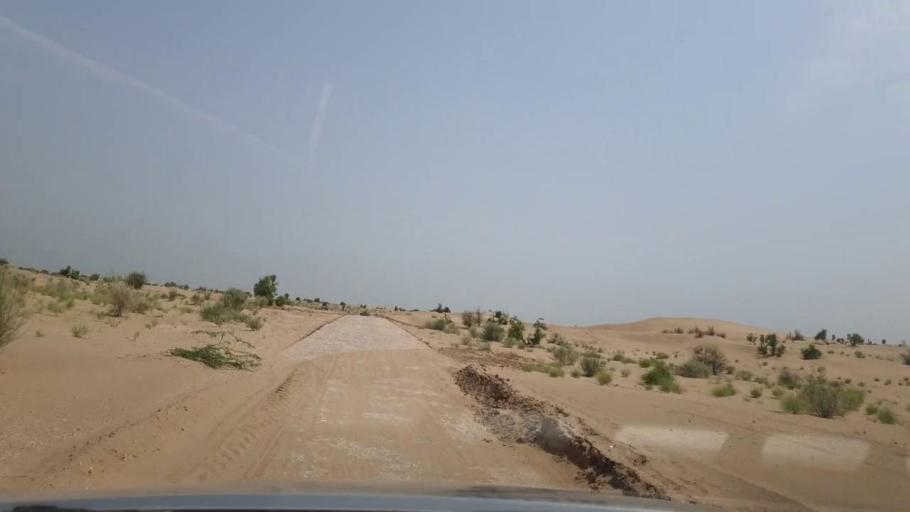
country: PK
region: Sindh
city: Pano Aqil
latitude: 27.5811
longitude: 69.1593
